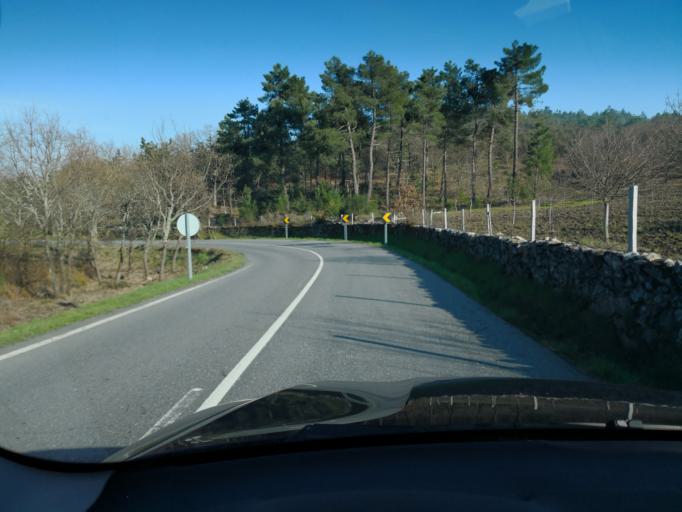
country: PT
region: Vila Real
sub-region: Sabrosa
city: Sabrosa
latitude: 41.3579
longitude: -7.6320
